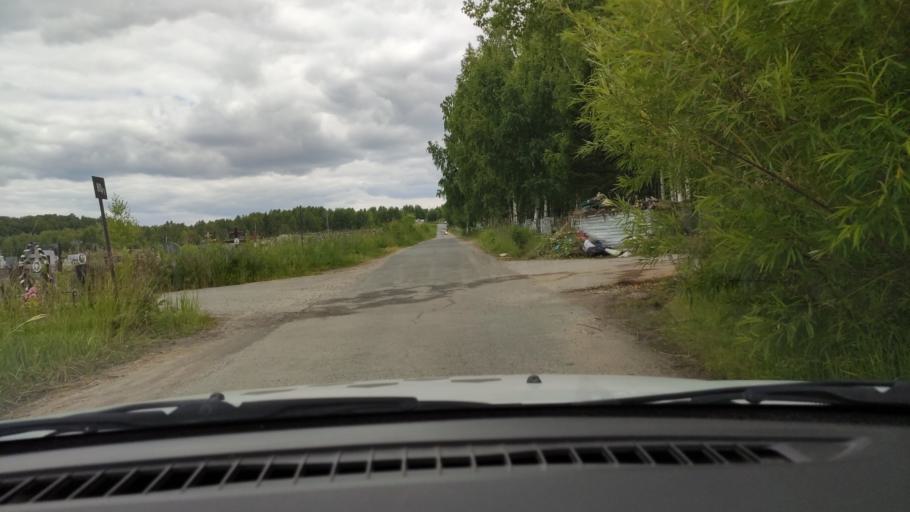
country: RU
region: Perm
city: Kondratovo
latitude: 58.0686
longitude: 56.1390
